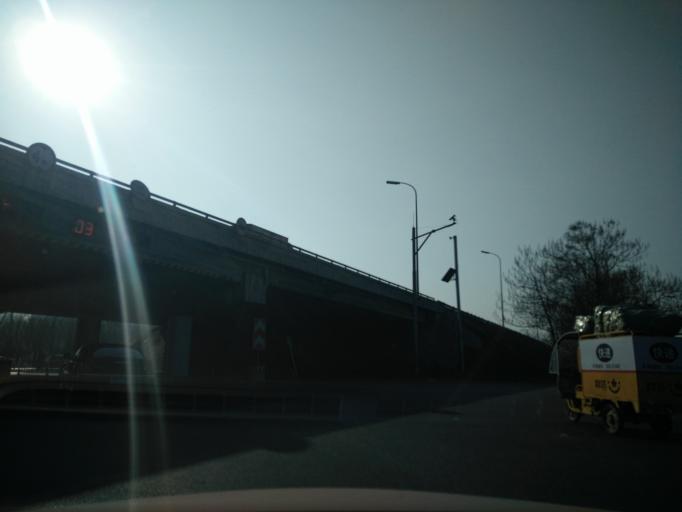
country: CN
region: Beijing
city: Jiugong
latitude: 39.8140
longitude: 116.4858
